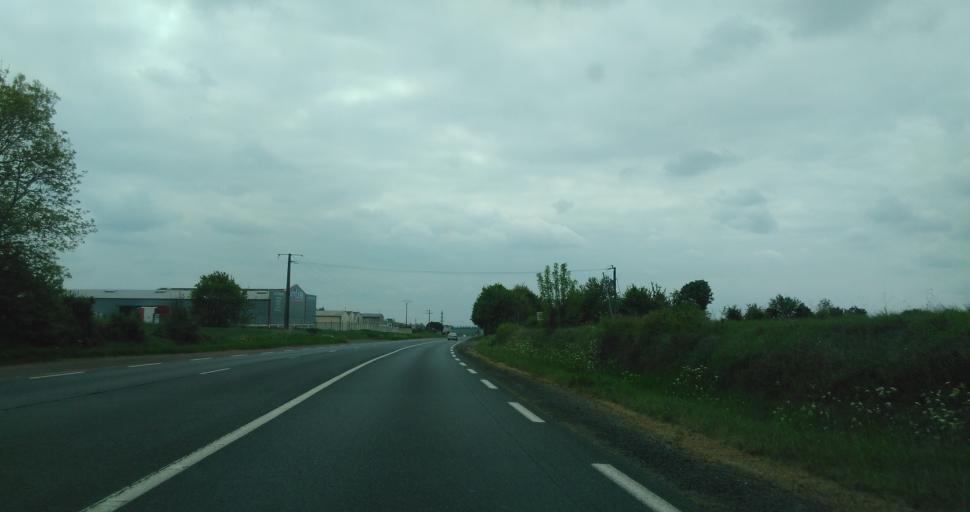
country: FR
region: Poitou-Charentes
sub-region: Departement des Deux-Sevres
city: Echire
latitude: 46.3682
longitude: -0.4272
